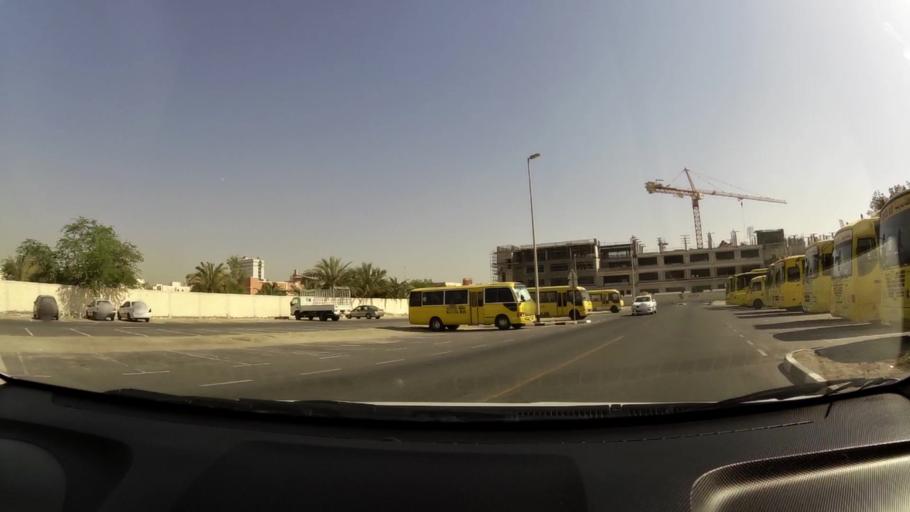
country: AE
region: Ash Shariqah
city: Sharjah
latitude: 25.2812
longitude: 55.3682
